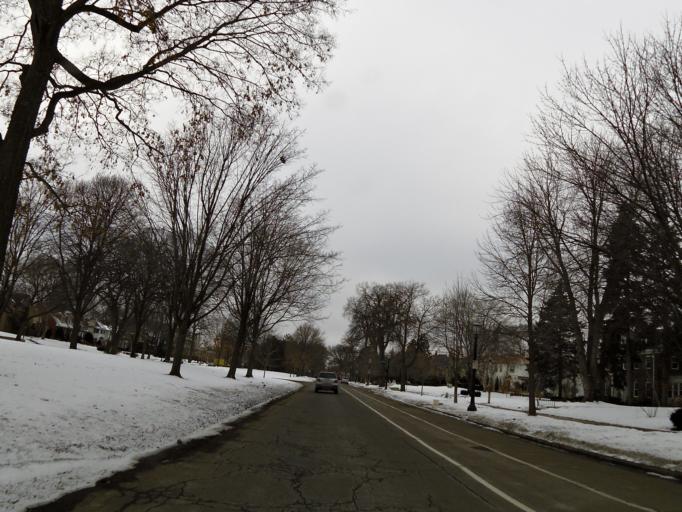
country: US
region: Minnesota
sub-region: Ramsey County
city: Falcon Heights
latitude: 44.9417
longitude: -93.1847
